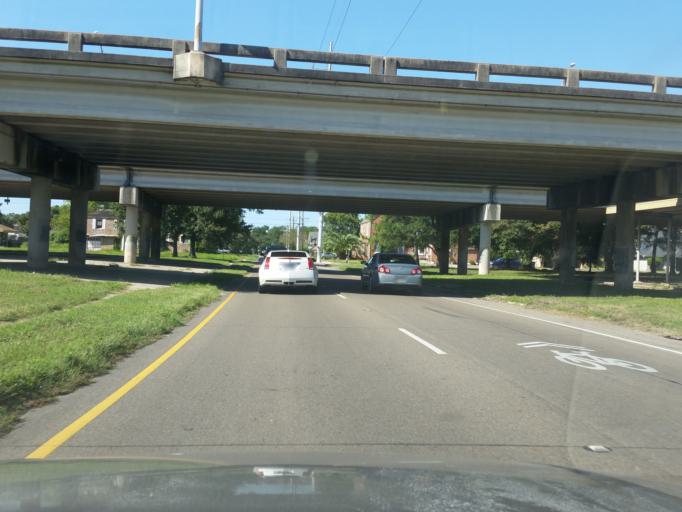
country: US
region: Louisiana
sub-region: Orleans Parish
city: New Orleans
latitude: 29.9905
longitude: -90.0656
